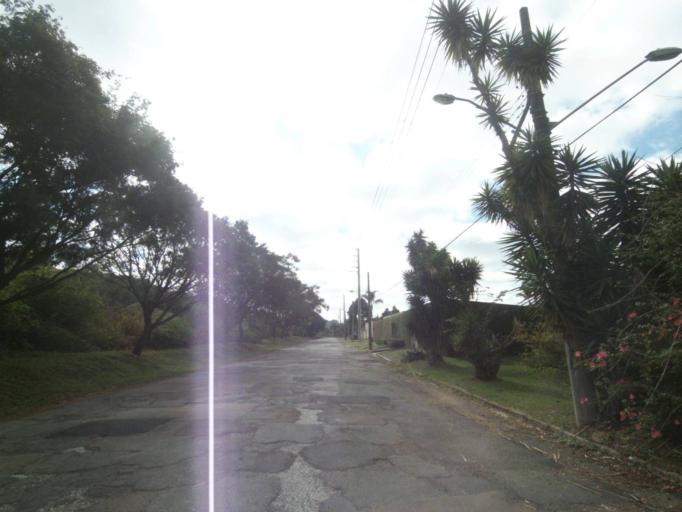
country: BR
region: Parana
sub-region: Curitiba
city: Curitiba
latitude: -25.4456
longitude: -49.3152
